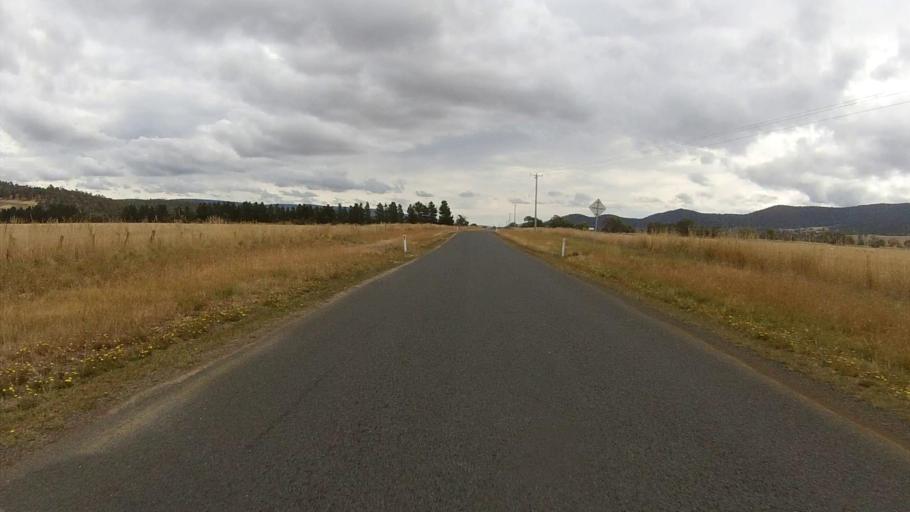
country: AU
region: Tasmania
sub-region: Northern Midlands
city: Evandale
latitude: -41.8250
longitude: 147.8414
